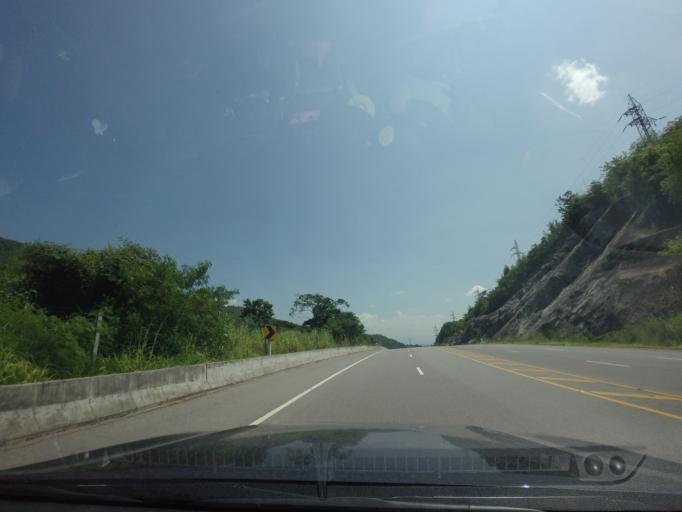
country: TH
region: Phetchabun
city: Lom Sak
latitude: 16.7734
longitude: 101.1317
